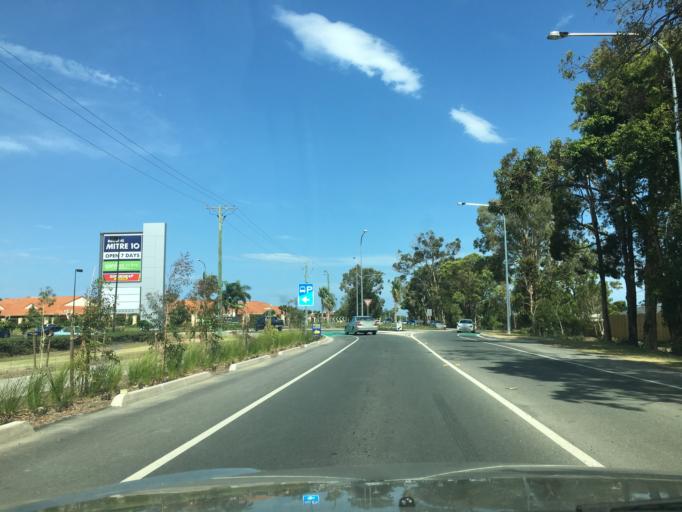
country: AU
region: Queensland
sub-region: Moreton Bay
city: Bongaree
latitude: -27.0658
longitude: 153.1578
